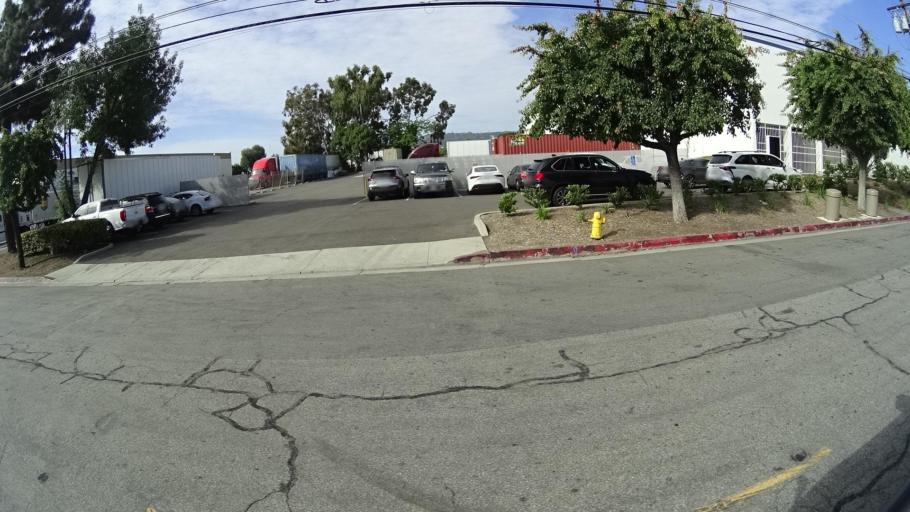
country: US
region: California
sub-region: Los Angeles County
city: La Puente
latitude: 34.0274
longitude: -117.9623
